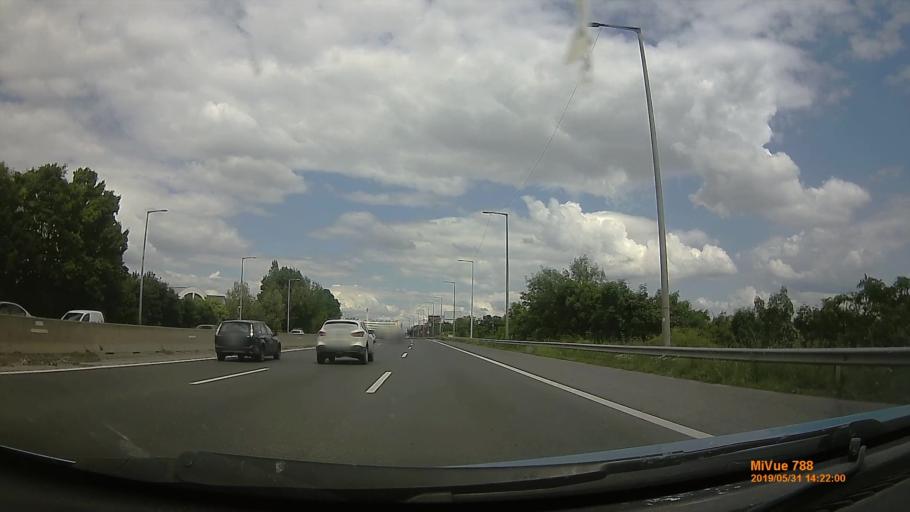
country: HU
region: Budapest
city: Budapest XII. keruelet
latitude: 47.4613
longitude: 19.0053
